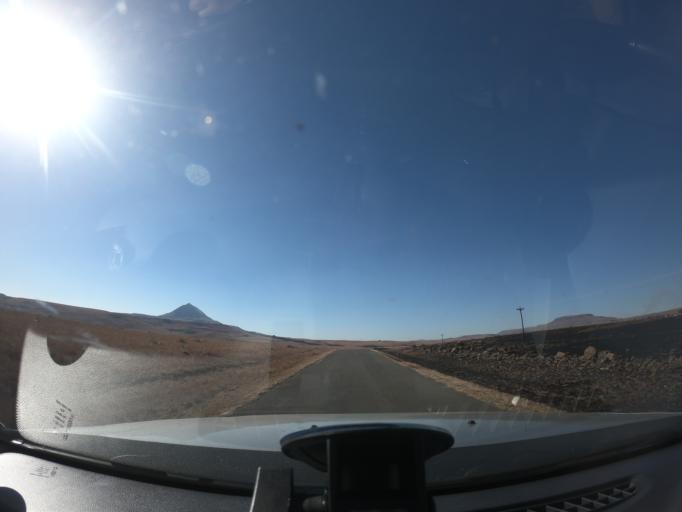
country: ZA
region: KwaZulu-Natal
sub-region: uMgungundlovu District Municipality
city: Impendle
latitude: -29.3877
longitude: 29.7278
